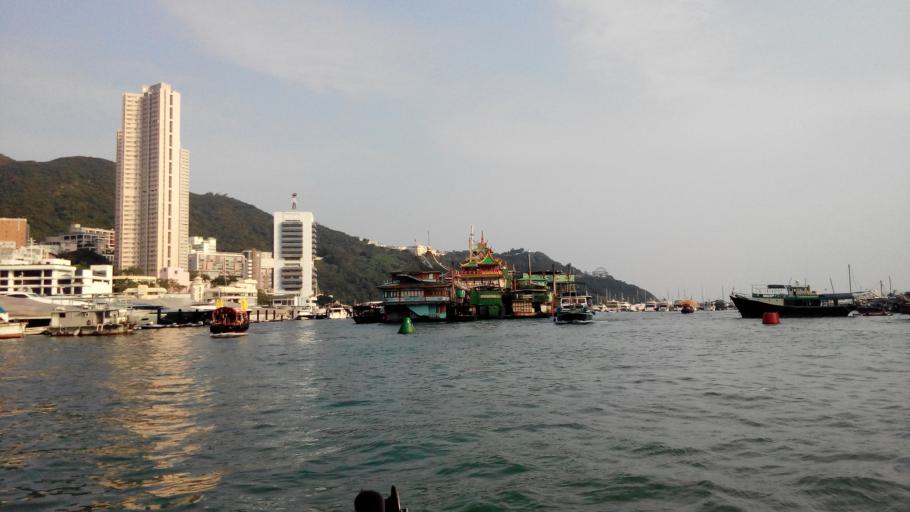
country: HK
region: Central and Western
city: Central
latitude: 22.2452
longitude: 114.1604
